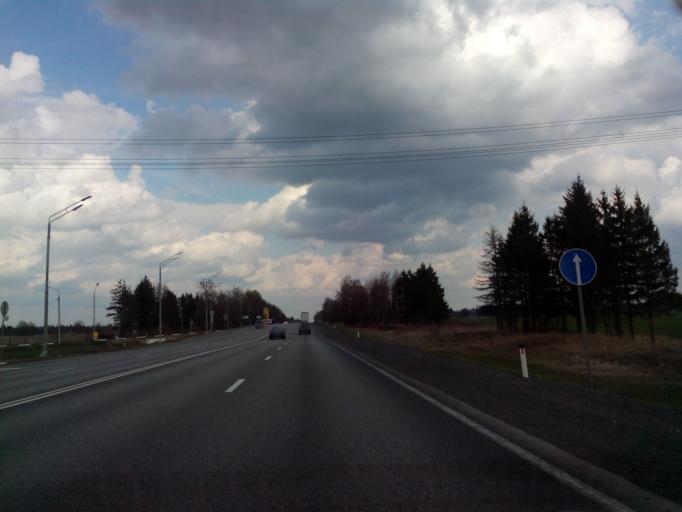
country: RU
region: Moskovskaya
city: Dorokhovo
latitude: 55.5103
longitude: 36.2496
